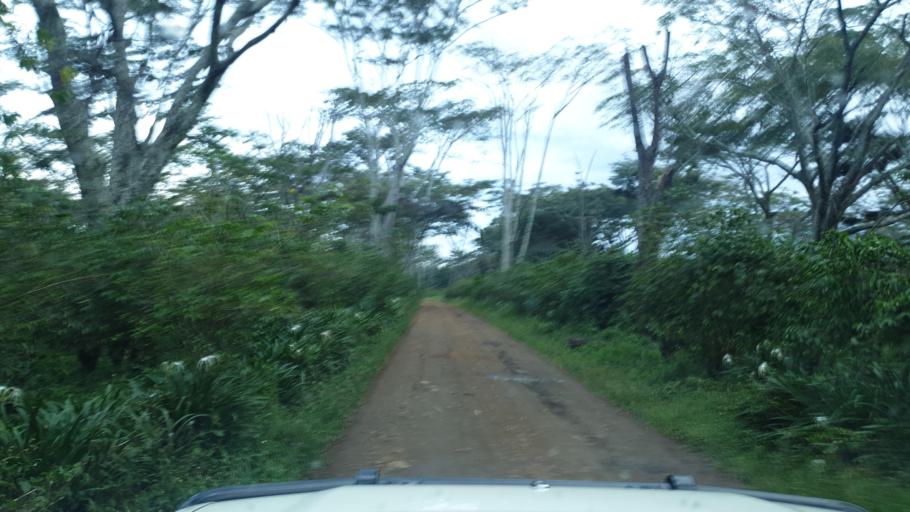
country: PG
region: Eastern Highlands
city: Goroka
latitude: -5.9621
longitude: 145.2722
